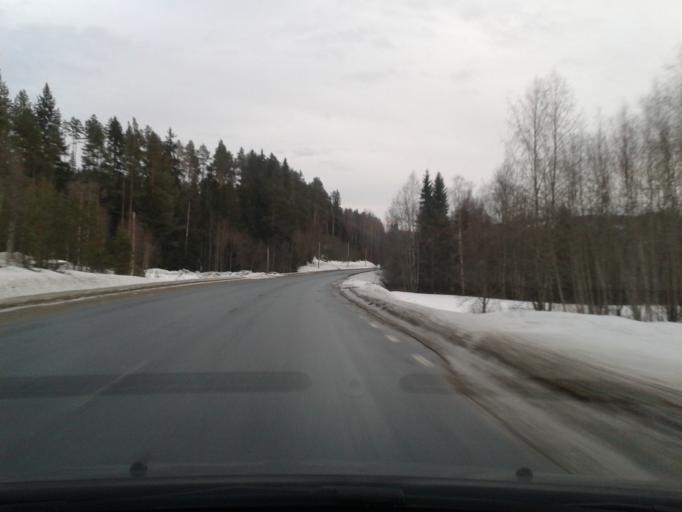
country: SE
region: Vaesternorrland
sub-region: Solleftea Kommun
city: Solleftea
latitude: 63.2048
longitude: 17.2325
